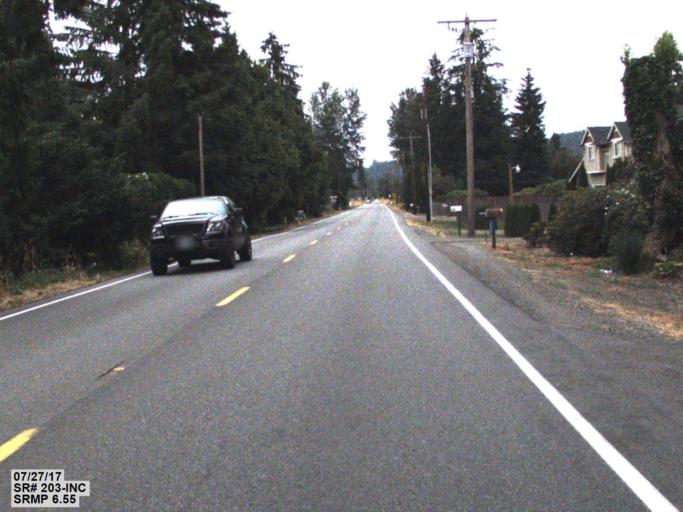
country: US
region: Washington
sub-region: King County
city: Carnation
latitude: 47.6559
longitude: -121.9111
